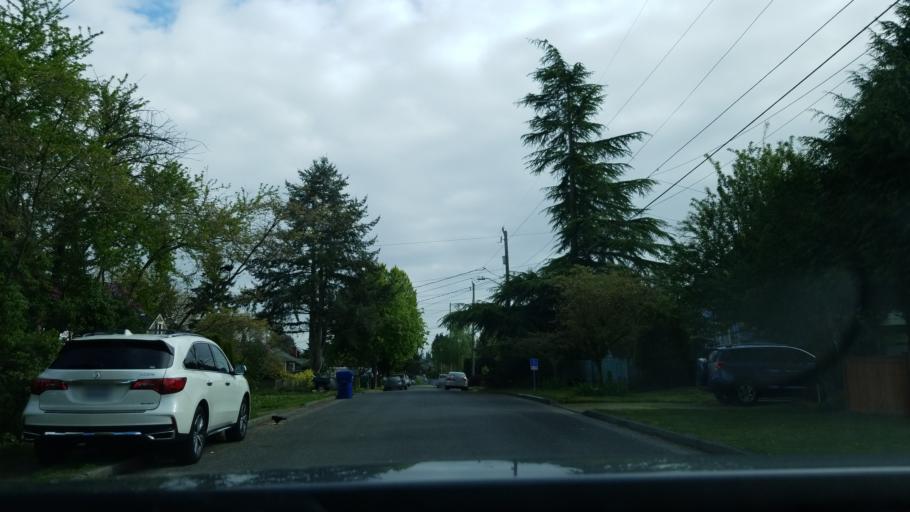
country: US
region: Washington
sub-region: King County
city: Shoreline
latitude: 47.6993
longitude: -122.3621
